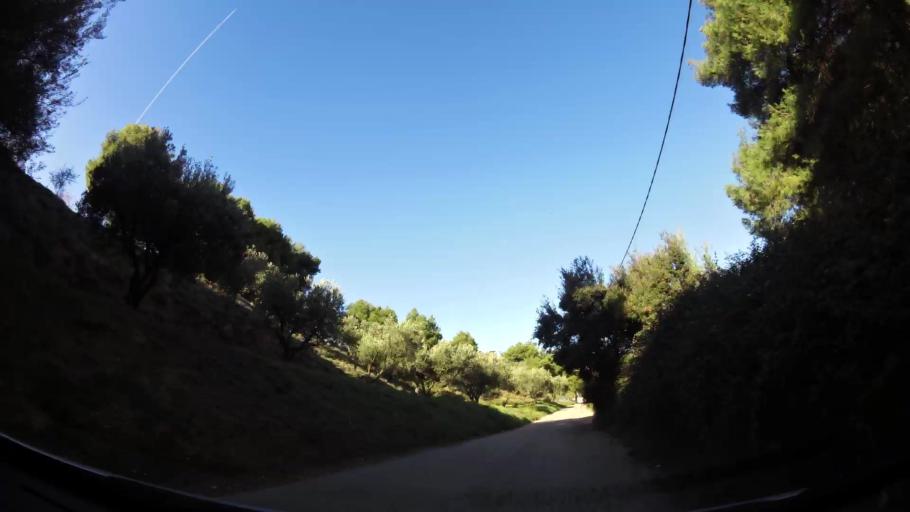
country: GR
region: Attica
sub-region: Nomarchia Anatolikis Attikis
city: Anoixi
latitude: 38.1367
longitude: 23.8475
